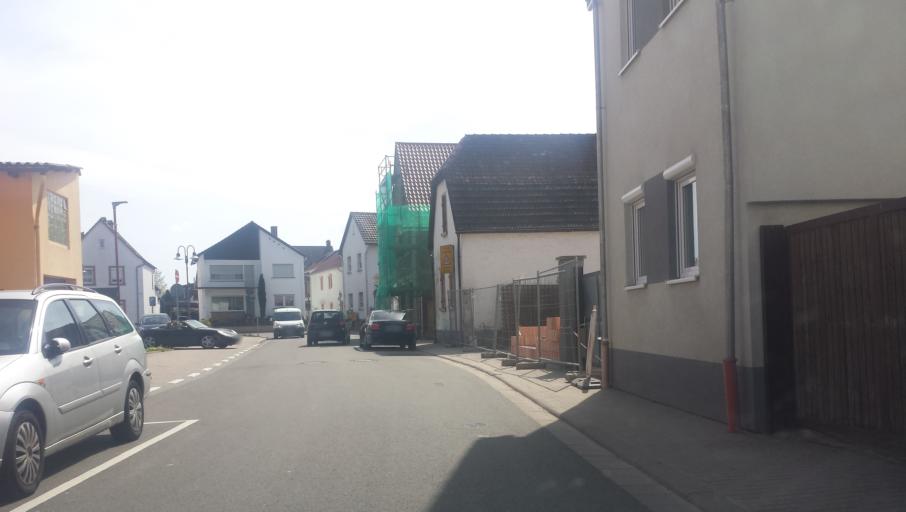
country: DE
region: Rheinland-Pfalz
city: Harthausen
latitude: 49.2956
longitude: 8.3439
